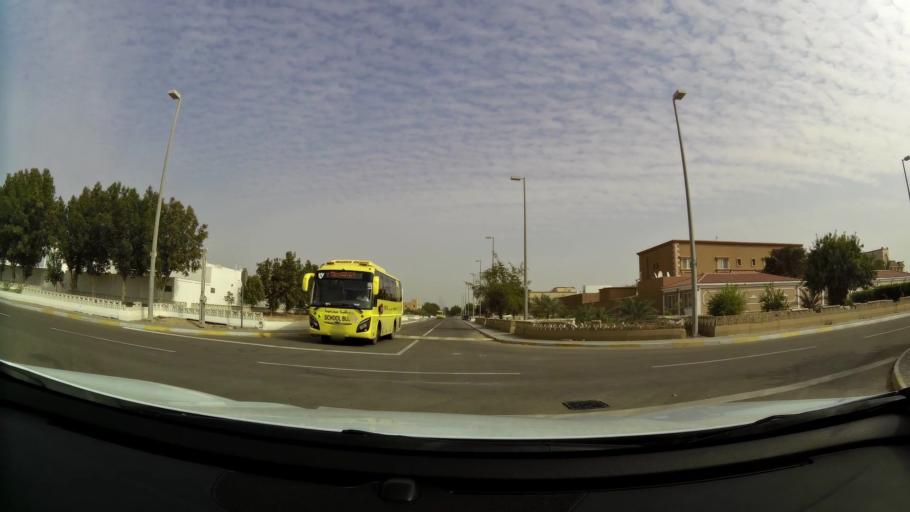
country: AE
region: Abu Dhabi
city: Abu Dhabi
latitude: 24.6093
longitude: 54.7029
